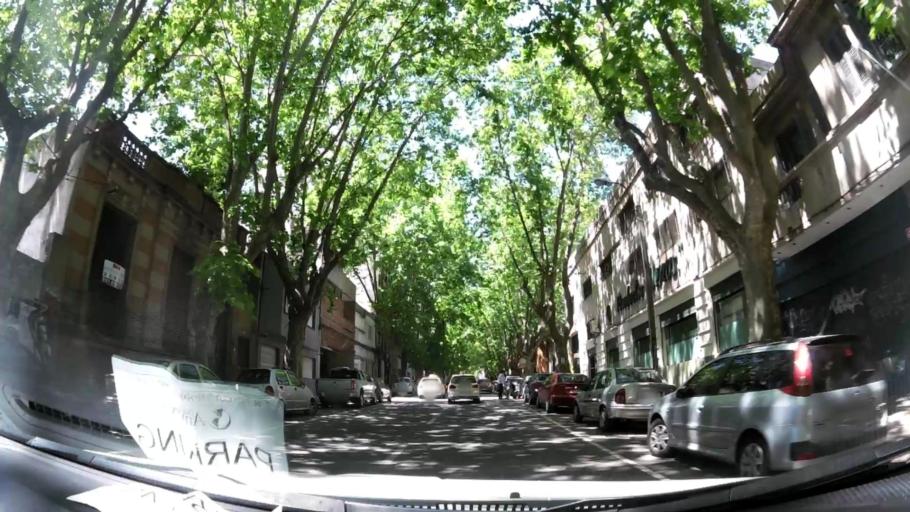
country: UY
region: Montevideo
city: Montevideo
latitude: -34.8973
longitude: -56.1696
